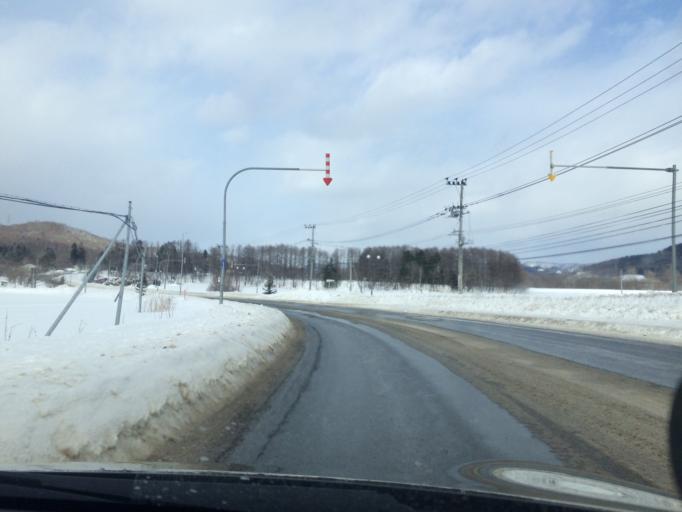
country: JP
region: Hokkaido
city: Shimo-furano
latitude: 42.9838
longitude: 142.3999
